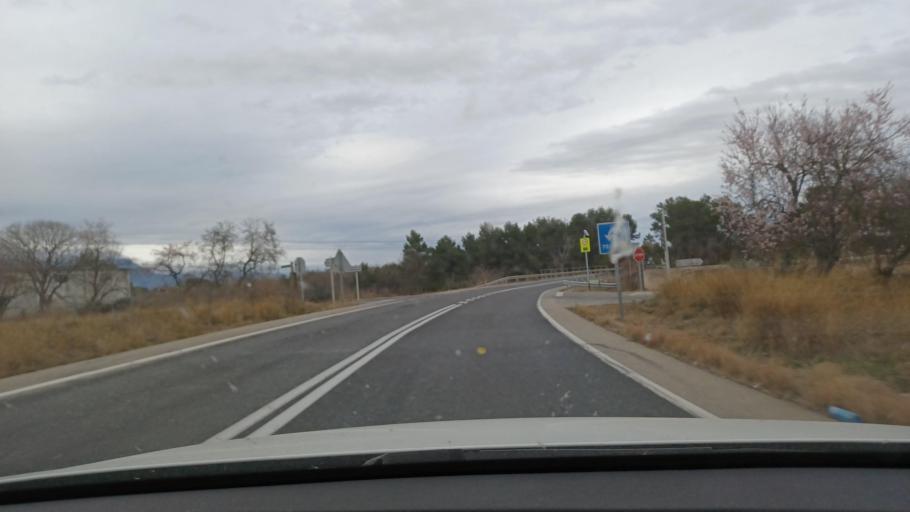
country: ES
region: Catalonia
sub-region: Provincia de Tarragona
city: Santa Barbara
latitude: 40.6806
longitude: 0.4582
